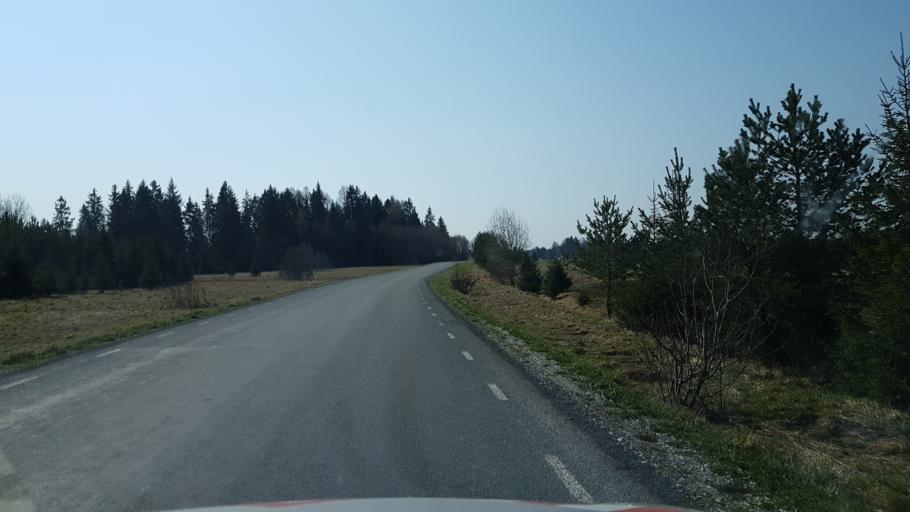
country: EE
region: Raplamaa
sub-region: Maerjamaa vald
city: Marjamaa
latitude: 58.8656
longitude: 24.3718
